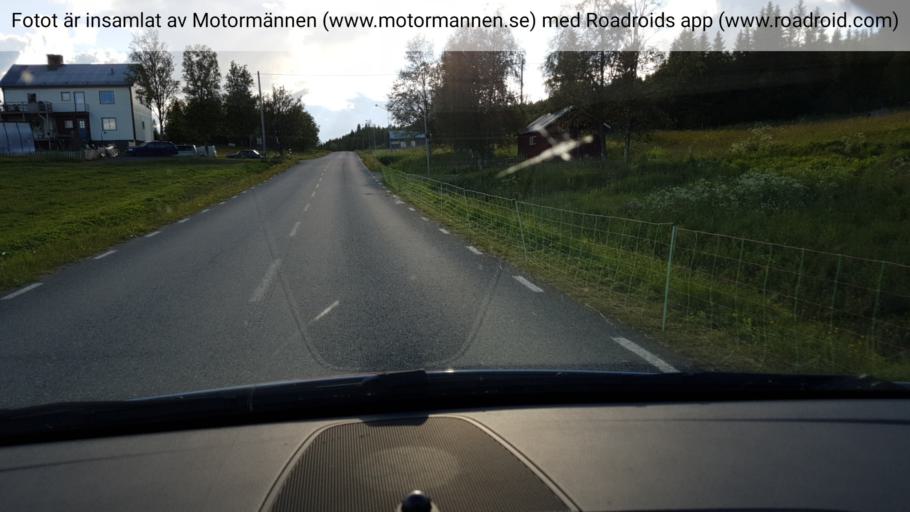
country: SE
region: Jaemtland
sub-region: Are Kommun
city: Are
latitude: 63.3156
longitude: 13.1012
